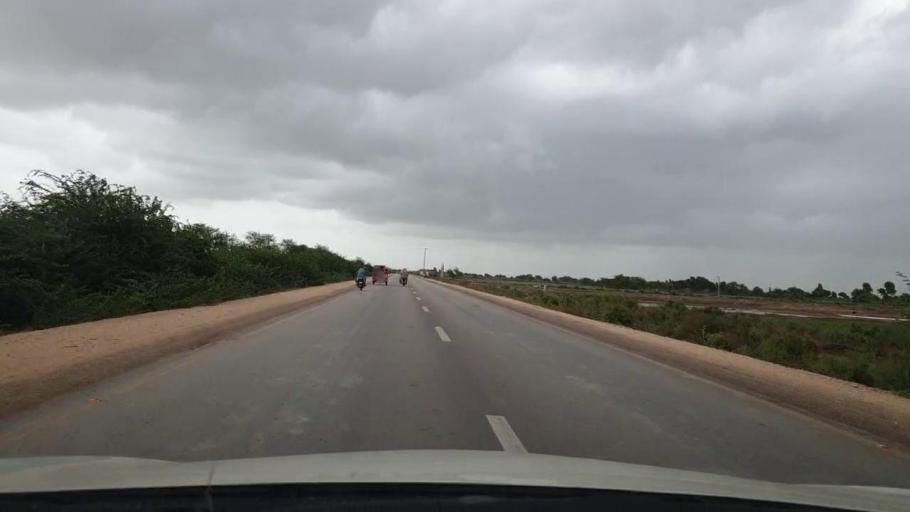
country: PK
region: Sindh
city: Mirpur Batoro
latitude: 24.6430
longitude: 68.4493
